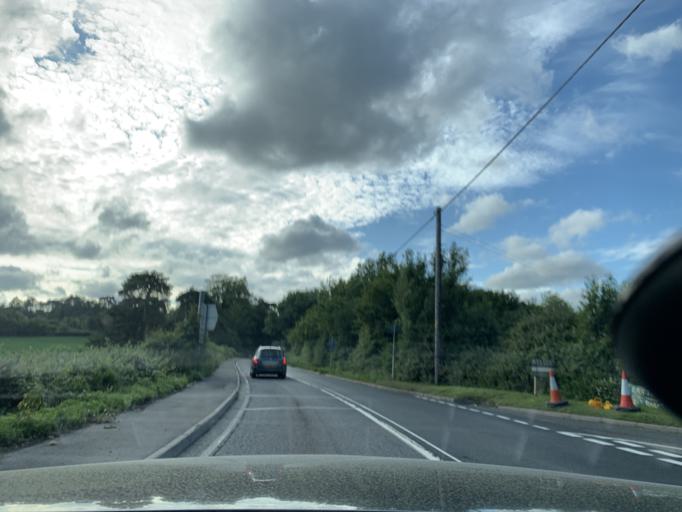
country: GB
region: England
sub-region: East Sussex
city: Battle
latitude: 50.9547
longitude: 0.5002
